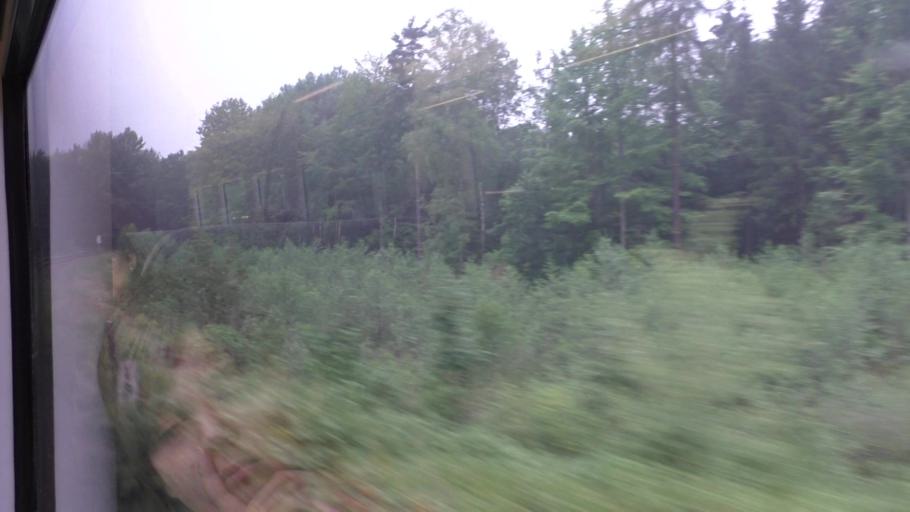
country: DE
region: Saxony
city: Berthelsdorf
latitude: 51.0842
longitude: 14.2529
